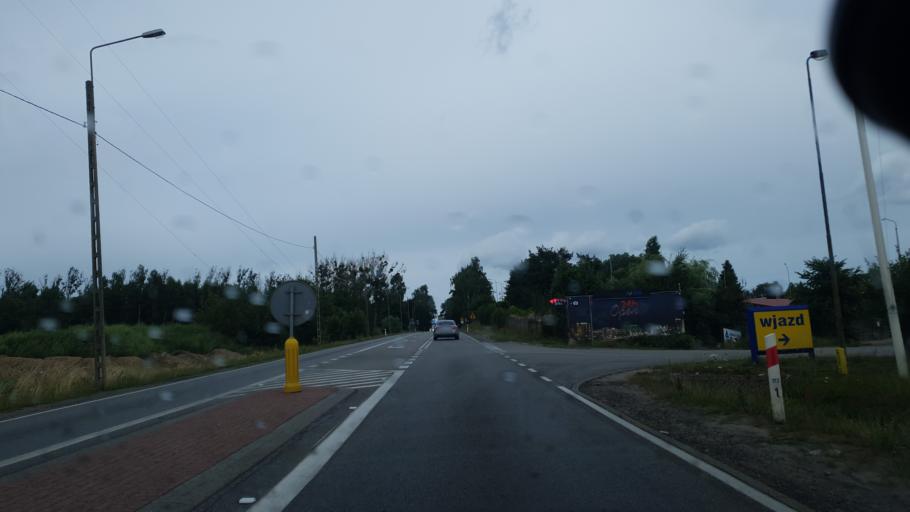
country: PL
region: Pomeranian Voivodeship
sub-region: Powiat kartuski
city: Chwaszczyno
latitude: 54.4502
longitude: 18.4363
